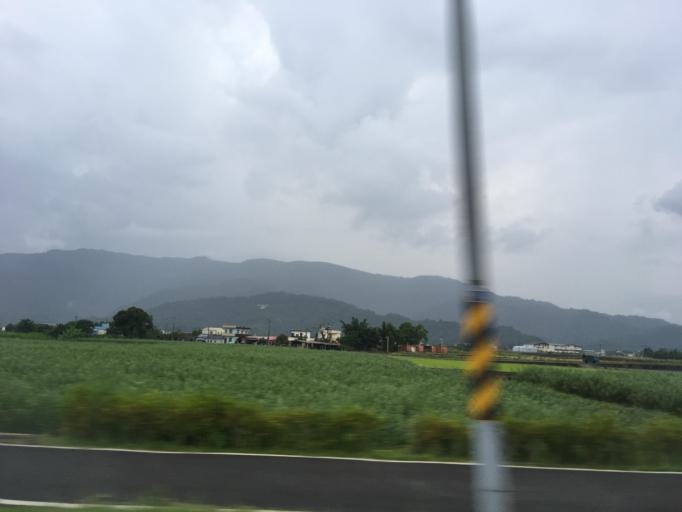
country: TW
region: Taiwan
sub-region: Yilan
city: Yilan
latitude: 24.6771
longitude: 121.6366
